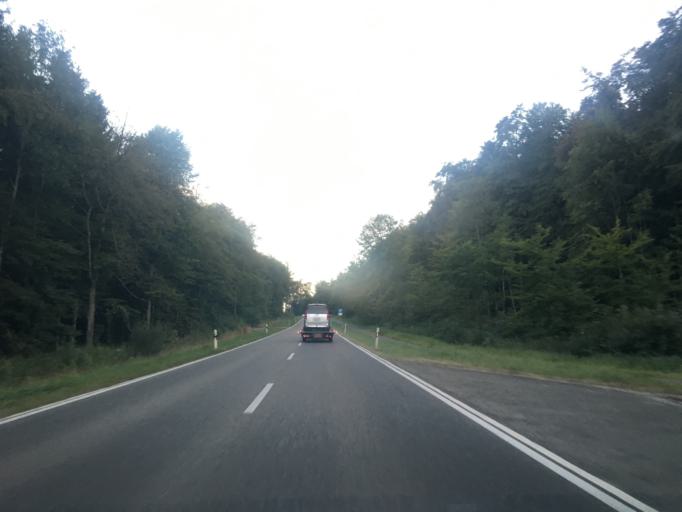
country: DE
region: Baden-Wuerttemberg
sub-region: Tuebingen Region
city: Gomadingen
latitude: 48.3699
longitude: 9.3209
